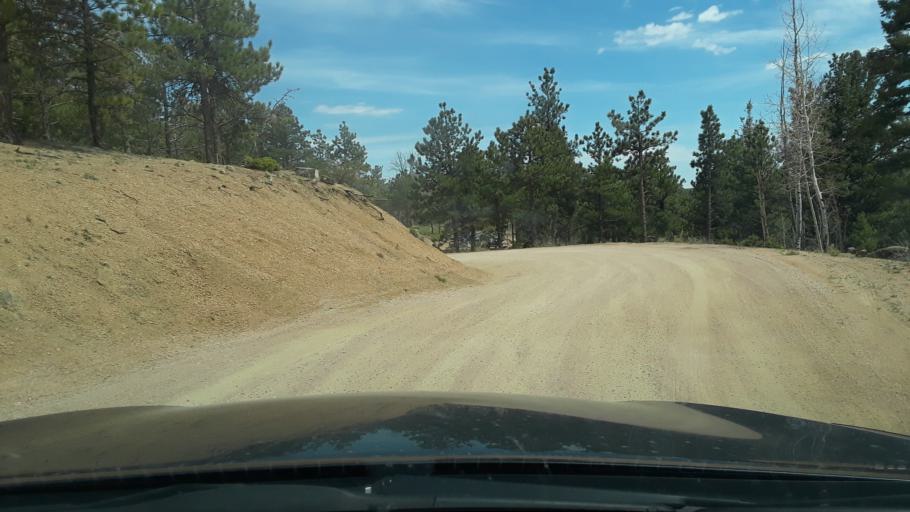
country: US
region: Colorado
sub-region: El Paso County
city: Palmer Lake
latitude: 39.0691
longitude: -104.9478
